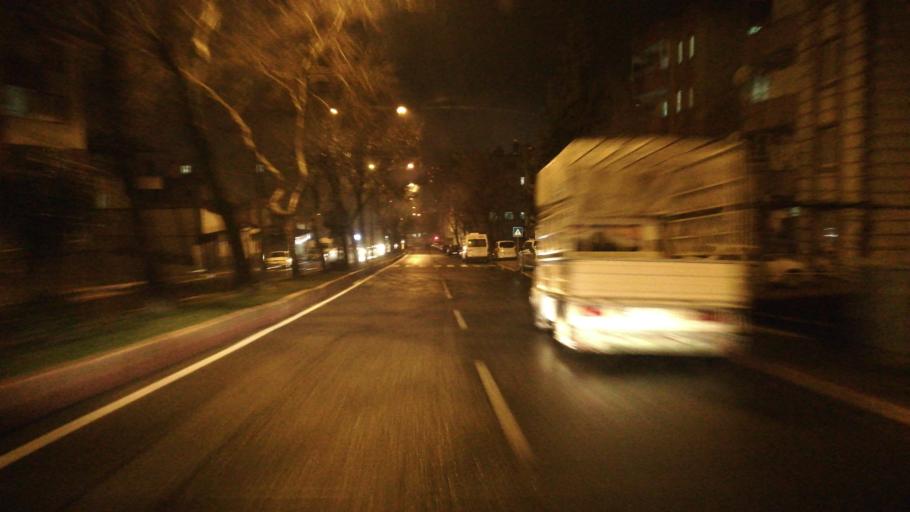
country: TR
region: Kahramanmaras
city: Kahramanmaras
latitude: 37.5884
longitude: 36.9368
